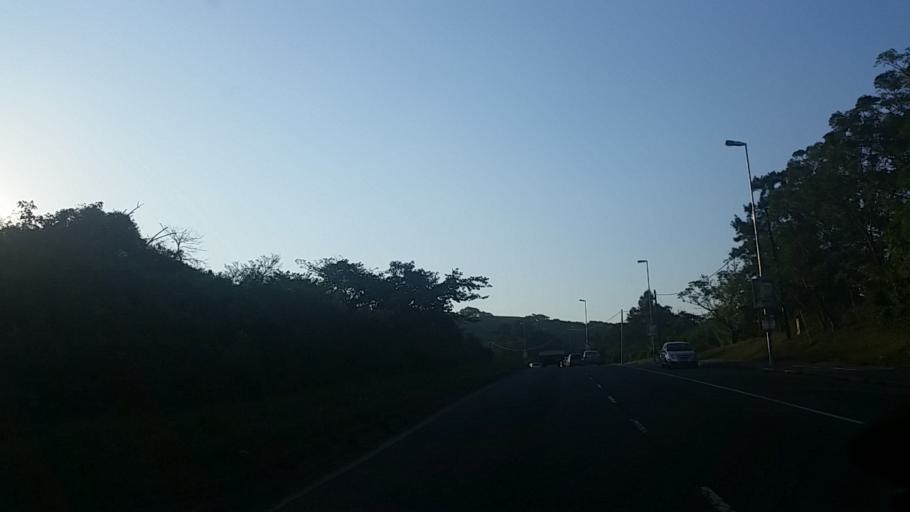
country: ZA
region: KwaZulu-Natal
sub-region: eThekwini Metropolitan Municipality
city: Berea
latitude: -29.8556
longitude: 30.9345
